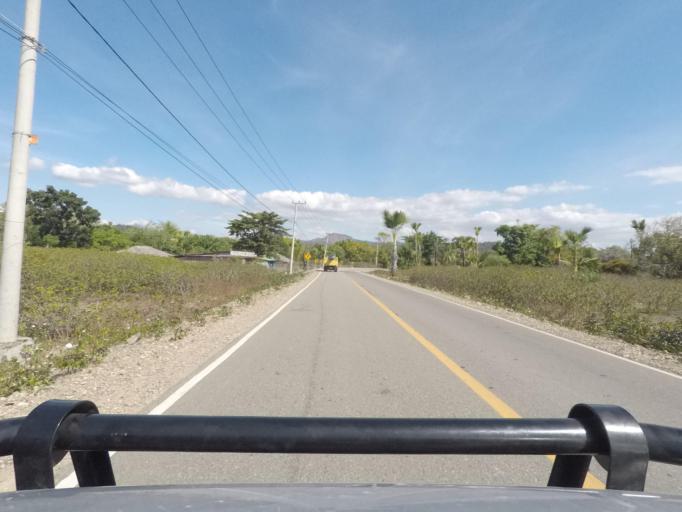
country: ID
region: East Nusa Tenggara
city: Atambua
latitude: -8.9402
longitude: 124.9789
